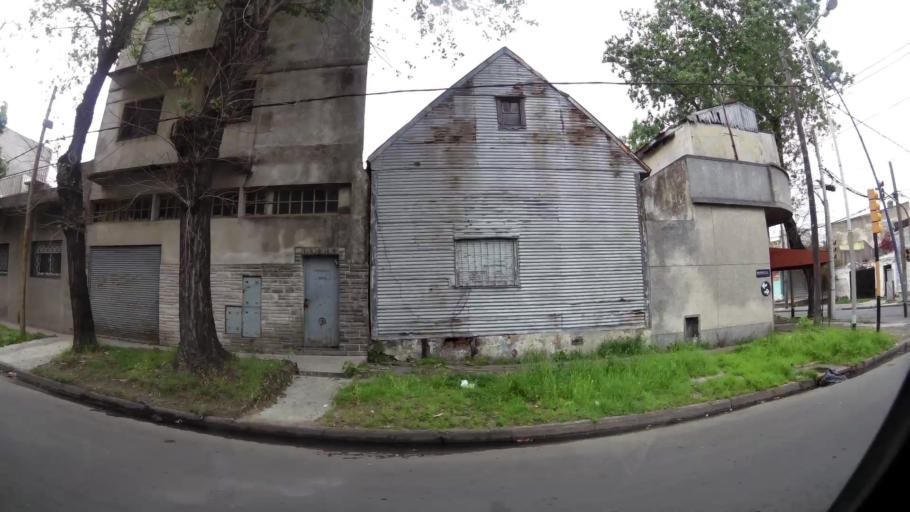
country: AR
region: Buenos Aires
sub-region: Partido de Avellaneda
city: Avellaneda
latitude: -34.6538
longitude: -58.3507
